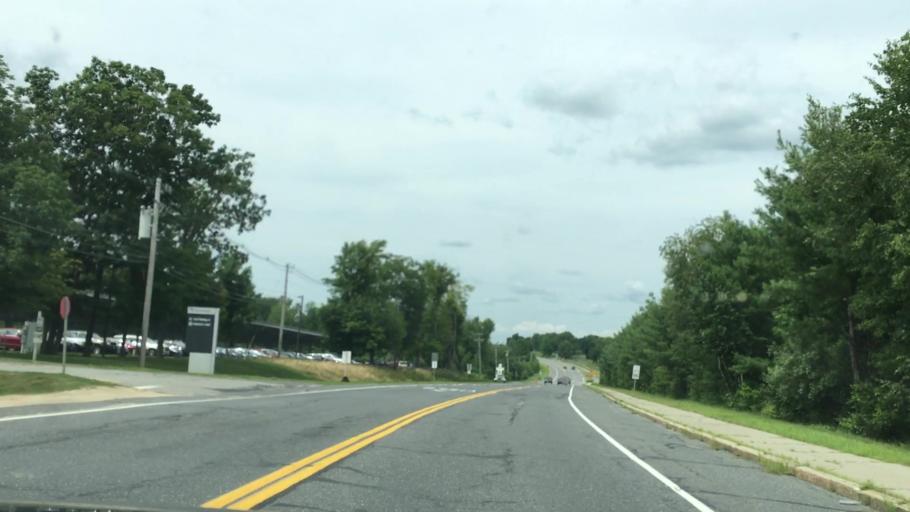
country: US
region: Massachusetts
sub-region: Worcester County
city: Gardner
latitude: 42.5881
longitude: -71.9867
